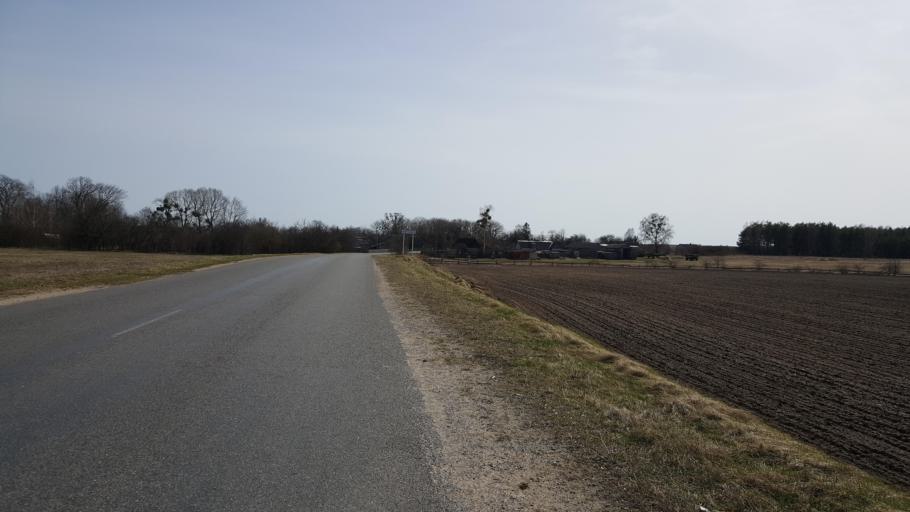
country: BY
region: Brest
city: Kamyanyuki
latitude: 52.4844
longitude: 23.8761
